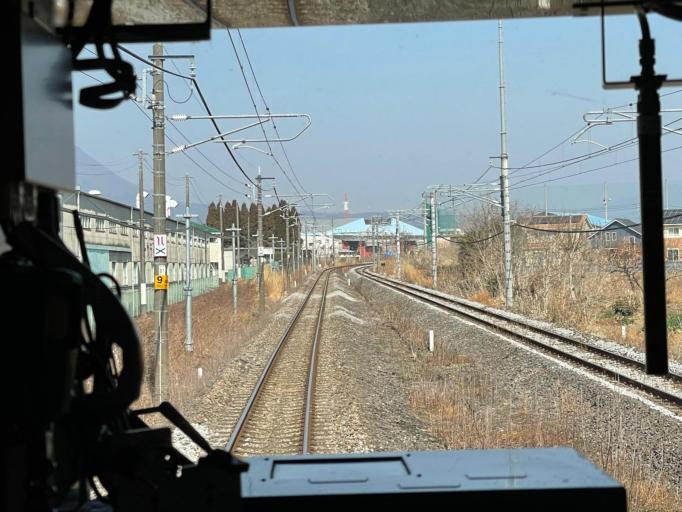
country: JP
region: Gunma
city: Maebashi-shi
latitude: 36.4062
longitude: 139.0371
